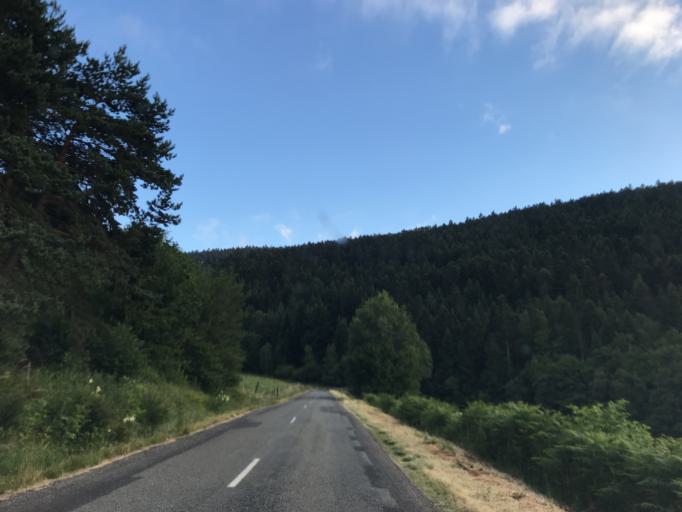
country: FR
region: Rhone-Alpes
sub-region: Departement de la Loire
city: Noiretable
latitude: 45.7555
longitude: 3.8272
